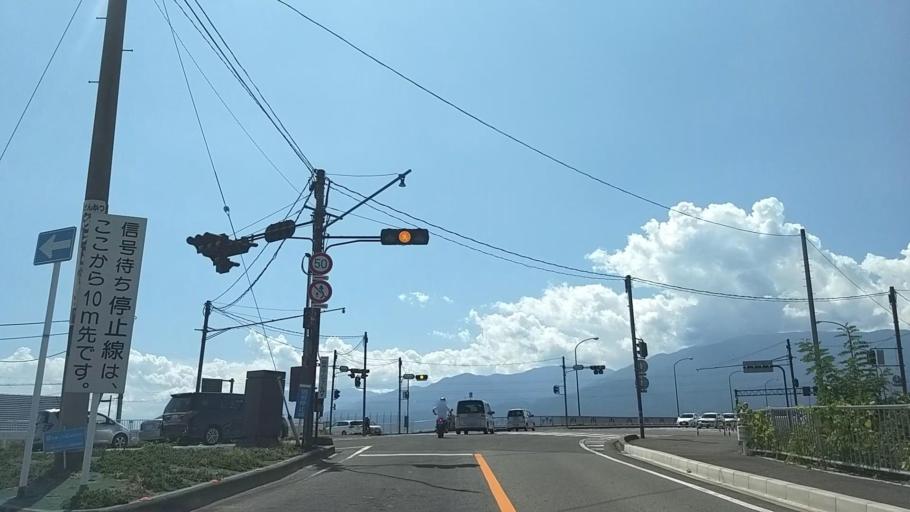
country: JP
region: Yamanashi
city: Ryuo
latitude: 35.6378
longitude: 138.5083
